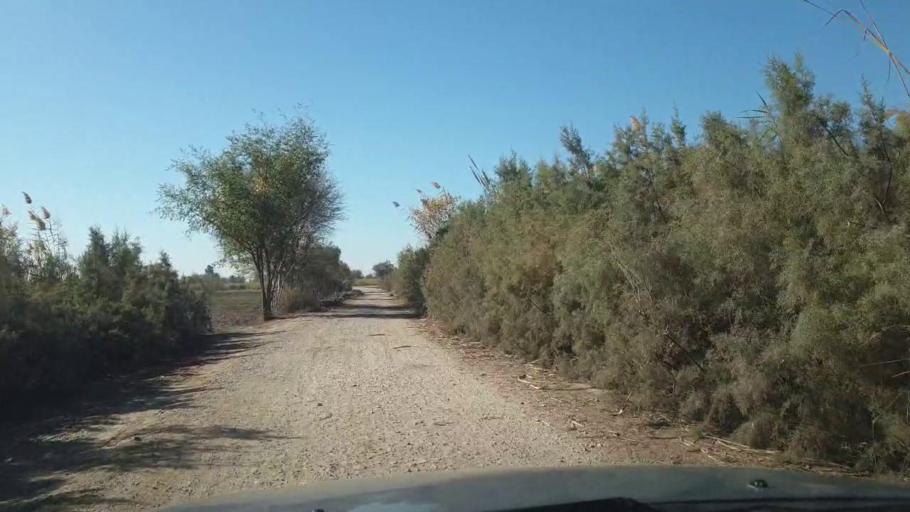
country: PK
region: Sindh
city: Ghotki
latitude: 28.0179
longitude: 69.2755
